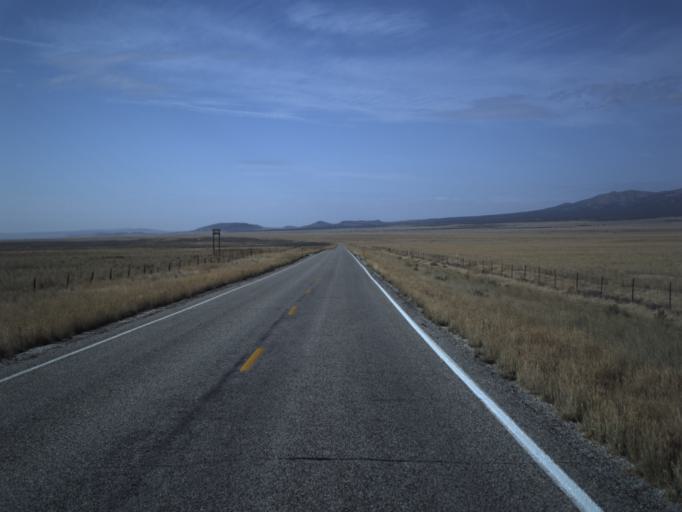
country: US
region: Idaho
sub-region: Oneida County
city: Malad City
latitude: 41.9597
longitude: -113.0672
